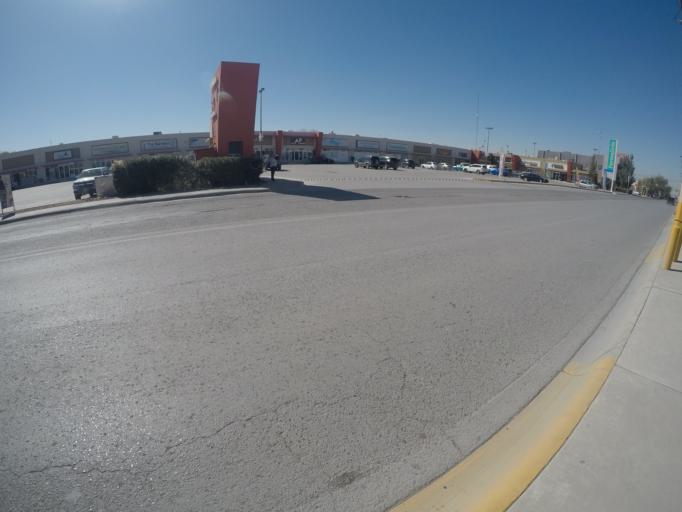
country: US
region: Texas
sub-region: El Paso County
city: Socorro
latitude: 31.6939
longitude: -106.3730
